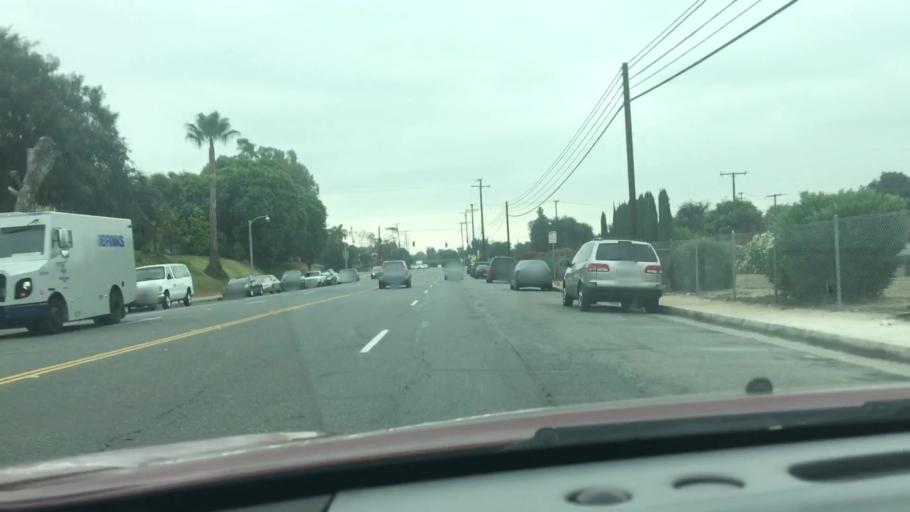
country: US
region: California
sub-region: Orange County
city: Fullerton
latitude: 33.8760
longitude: -117.9534
